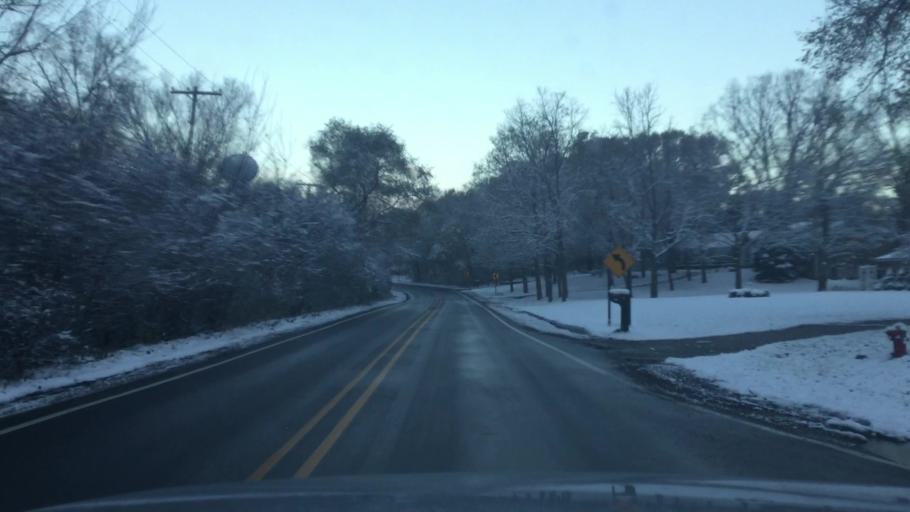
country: US
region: Michigan
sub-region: Oakland County
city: West Bloomfield Township
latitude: 42.5912
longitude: -83.4241
